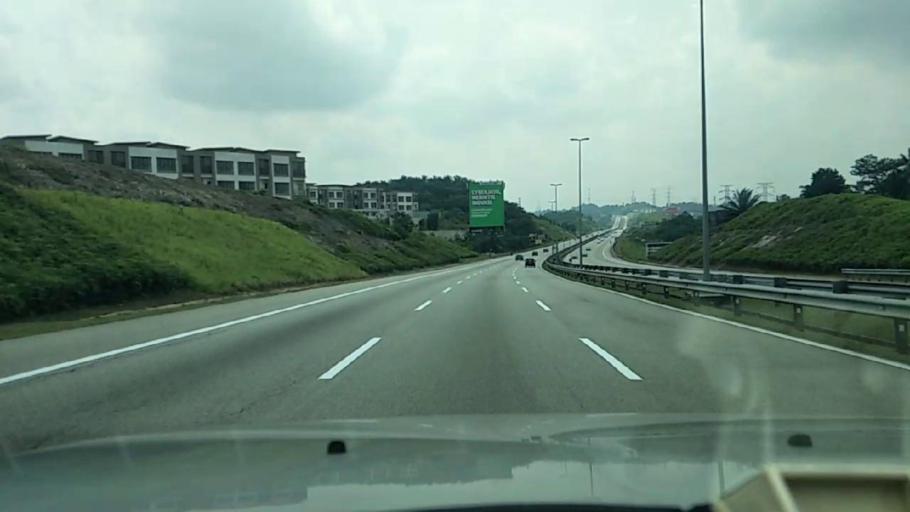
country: MY
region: Putrajaya
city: Putrajaya
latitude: 2.9666
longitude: 101.6588
